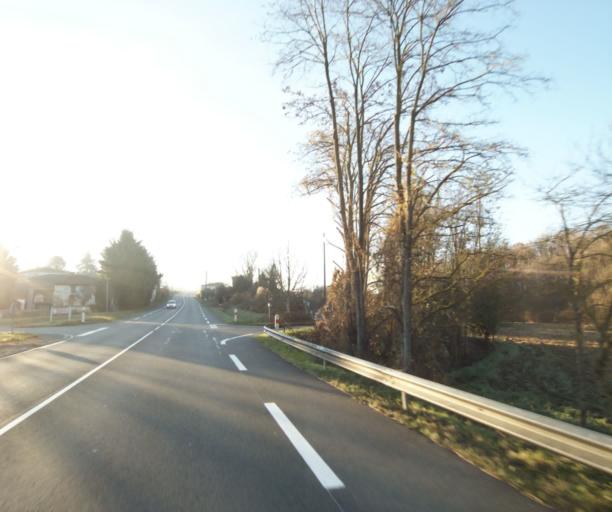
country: FR
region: Poitou-Charentes
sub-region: Departement de la Charente-Maritime
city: Cherac
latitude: 45.7188
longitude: -0.4950
